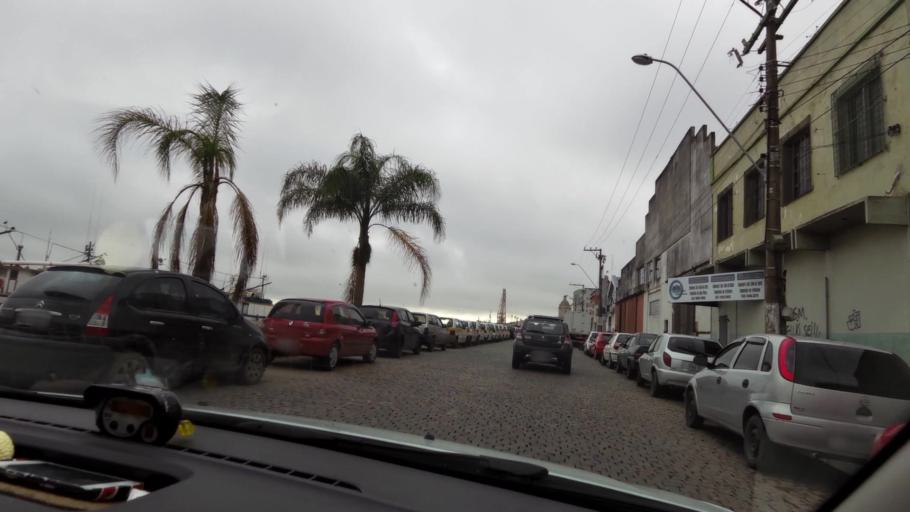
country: BR
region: Rio Grande do Sul
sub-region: Rio Grande
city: Rio Grande
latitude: -32.0346
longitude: -52.0918
